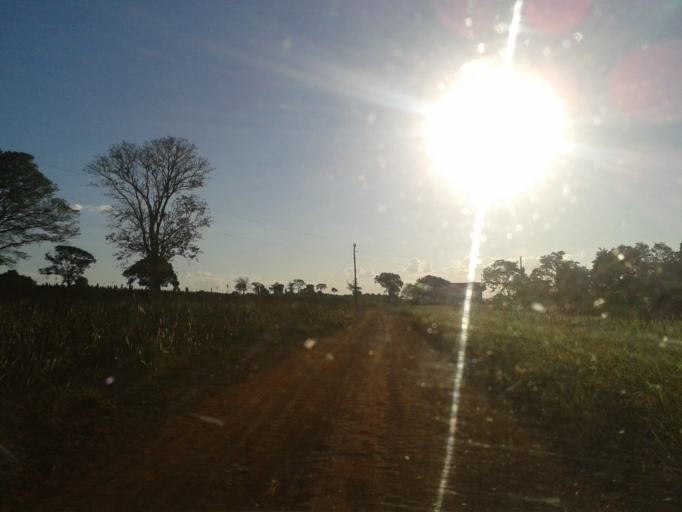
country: BR
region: Minas Gerais
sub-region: Centralina
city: Centralina
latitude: -18.6074
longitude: -49.3066
